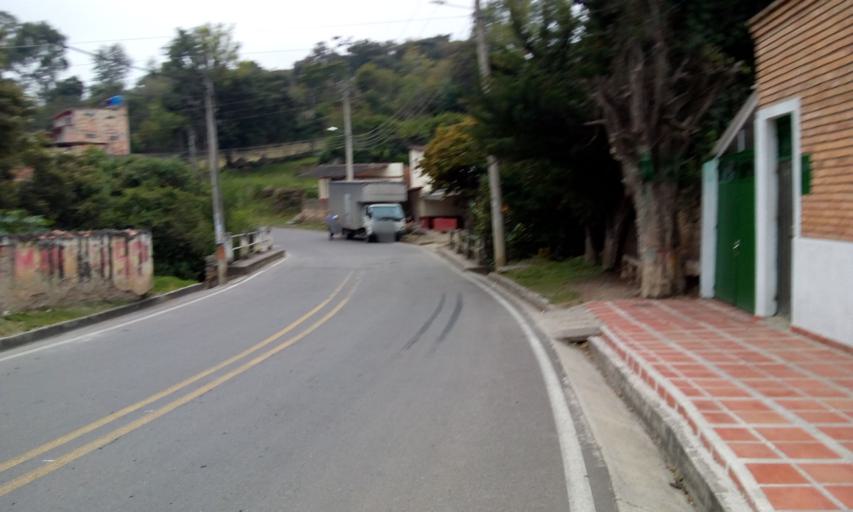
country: CO
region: Boyaca
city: Tipacoque
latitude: 6.4176
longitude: -72.6930
